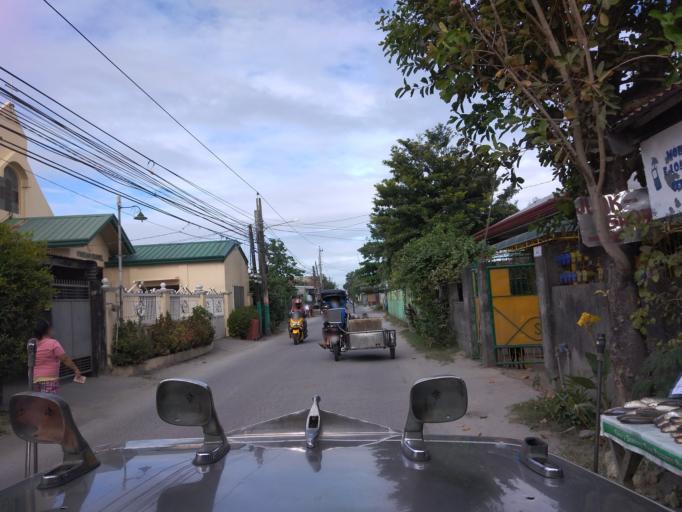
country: PH
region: Central Luzon
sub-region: Province of Pampanga
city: Mexico
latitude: 15.0689
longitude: 120.7157
